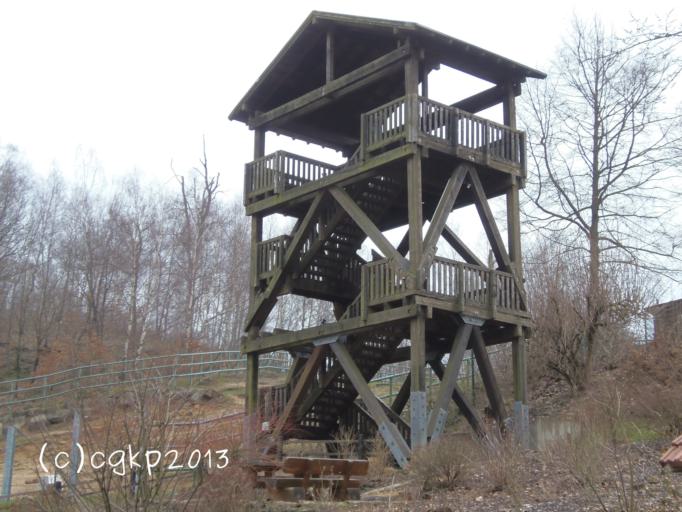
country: DE
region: Saarland
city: Neunkirchen
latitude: 49.3458
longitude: 7.2071
